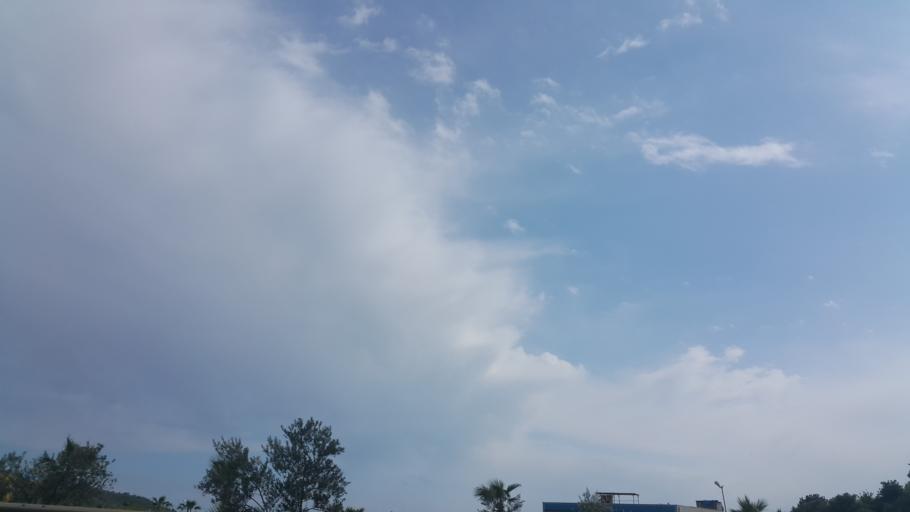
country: TR
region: Mersin
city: Tarsus
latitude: 36.9469
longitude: 34.7932
